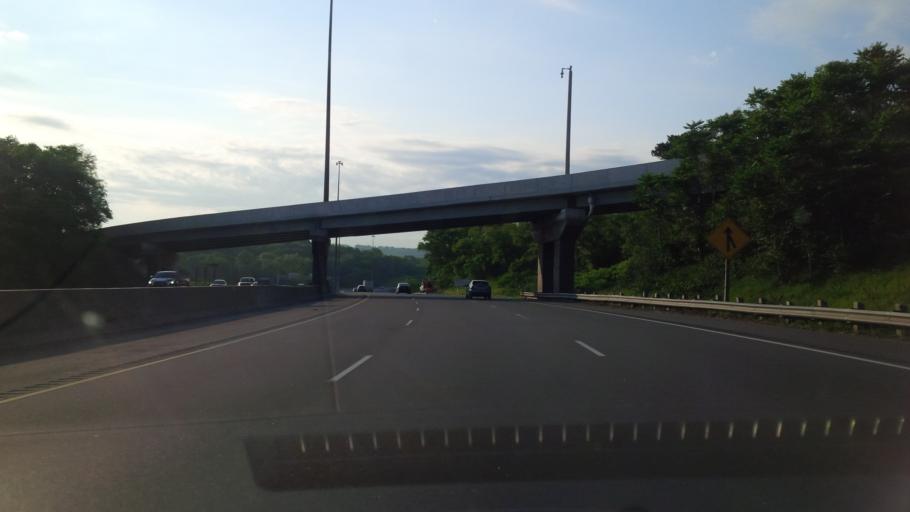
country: CA
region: Ontario
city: Hamilton
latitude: 43.2821
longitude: -79.8927
